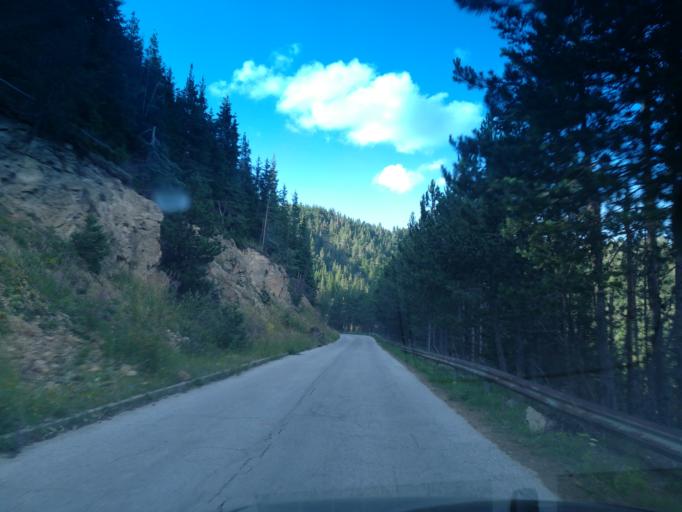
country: BG
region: Smolyan
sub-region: Obshtina Chepelare
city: Chepelare
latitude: 41.6844
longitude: 24.7525
